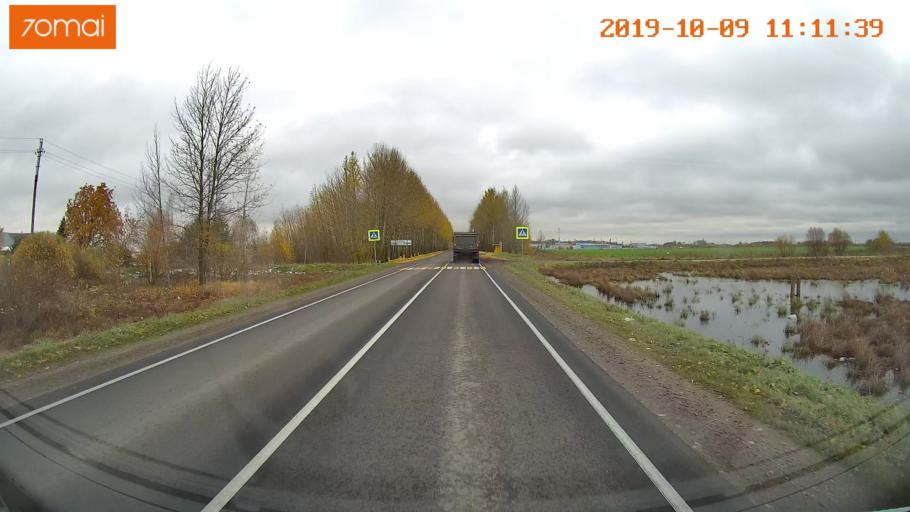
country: RU
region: Vologda
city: Vologda
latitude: 59.1701
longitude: 39.8226
